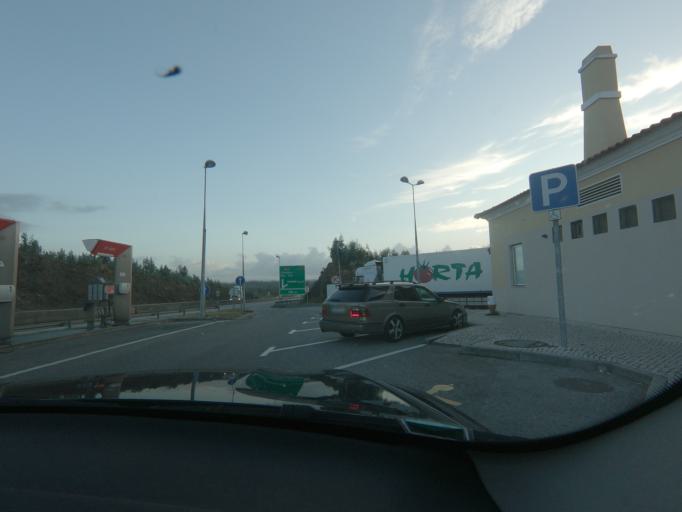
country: PT
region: Viseu
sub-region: Santa Comba Dao
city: Santa Comba Dao
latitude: 40.3491
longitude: -8.1731
